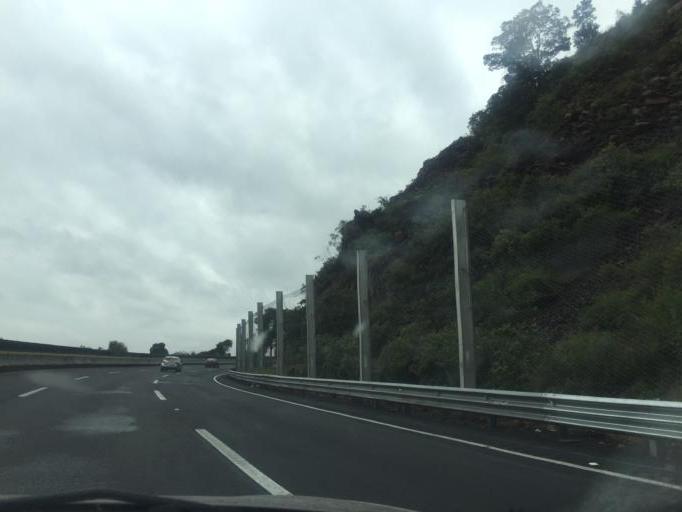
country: MX
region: Mexico City
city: Xochimilco
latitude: 19.2247
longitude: -99.1363
